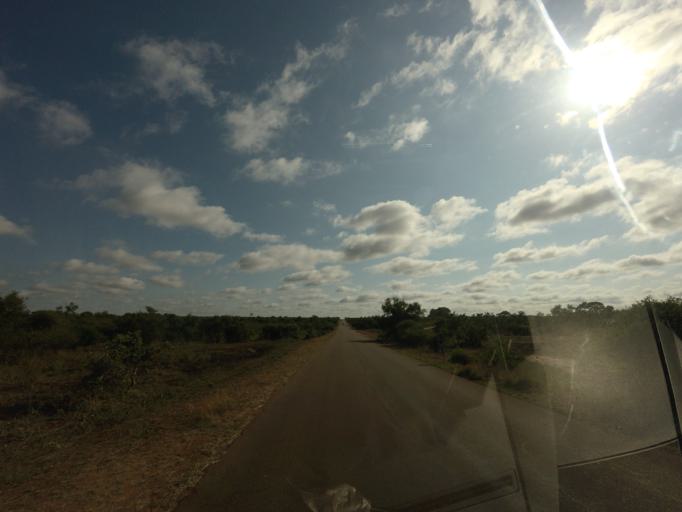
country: ZA
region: Mpumalanga
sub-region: Ehlanzeni District
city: Komatipoort
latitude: -25.1579
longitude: 31.9324
